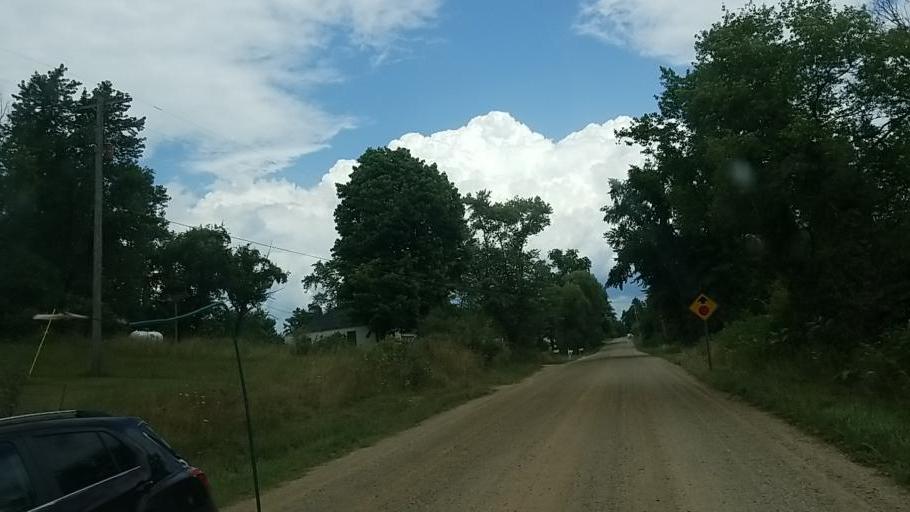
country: US
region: Michigan
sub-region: Kent County
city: Walker
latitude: 43.0164
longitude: -85.8096
